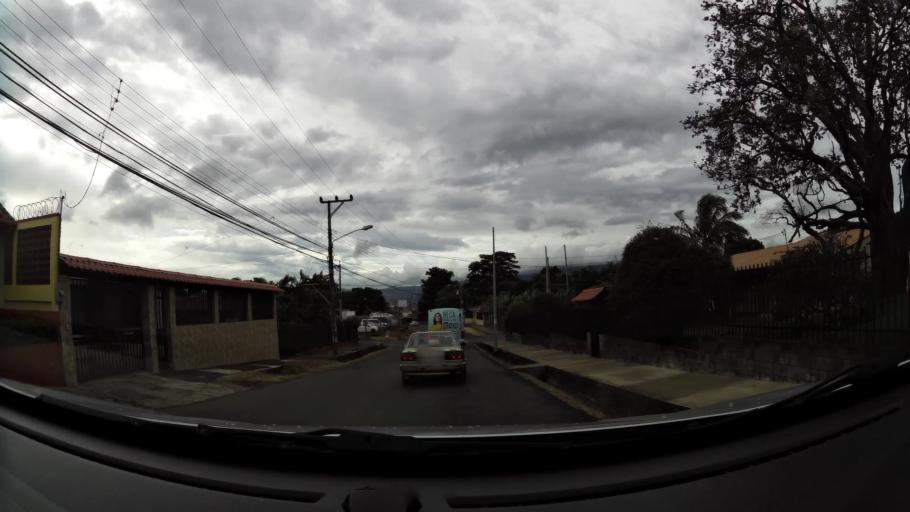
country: CR
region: San Jose
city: San Juan
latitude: 9.9772
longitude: -84.0899
